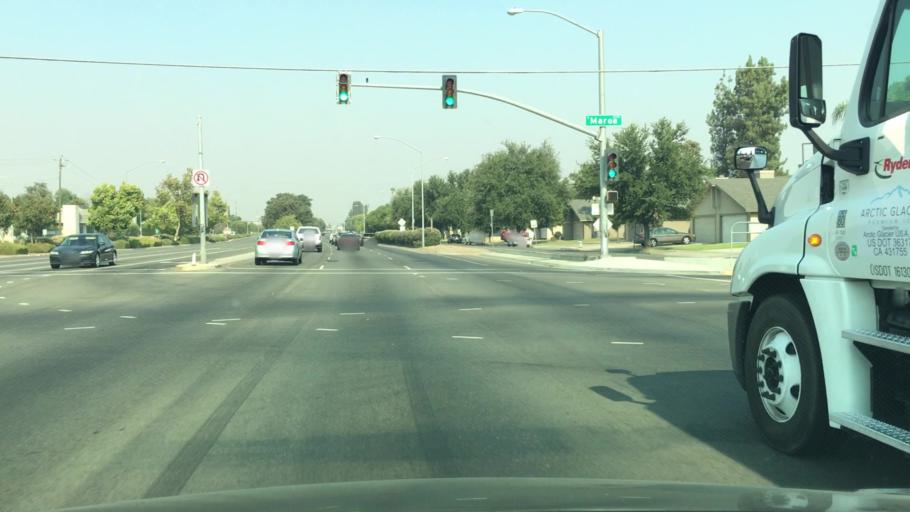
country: US
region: California
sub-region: Fresno County
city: Fresno
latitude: 36.8370
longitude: -119.7993
